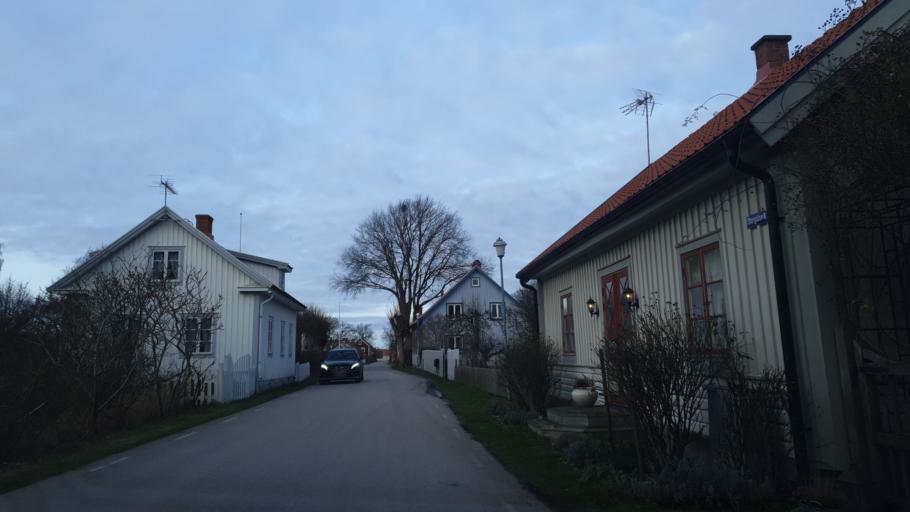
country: SE
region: Kalmar
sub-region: Torsas Kommun
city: Torsas
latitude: 56.2569
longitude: 16.0425
